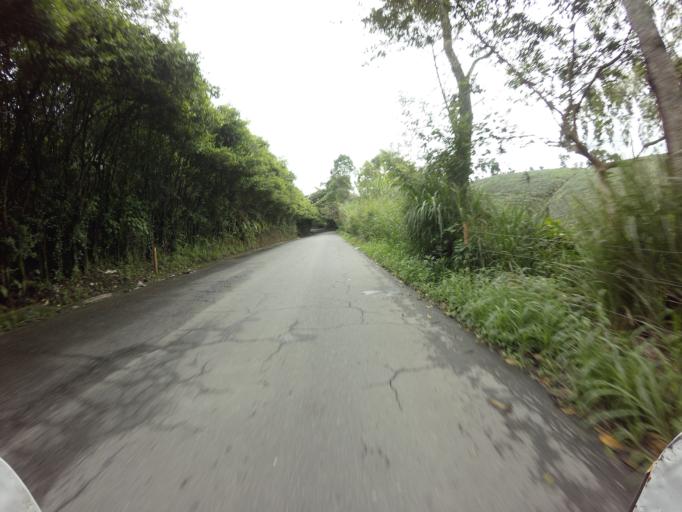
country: CO
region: Valle del Cauca
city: Alcala
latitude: 4.6800
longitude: -75.7775
